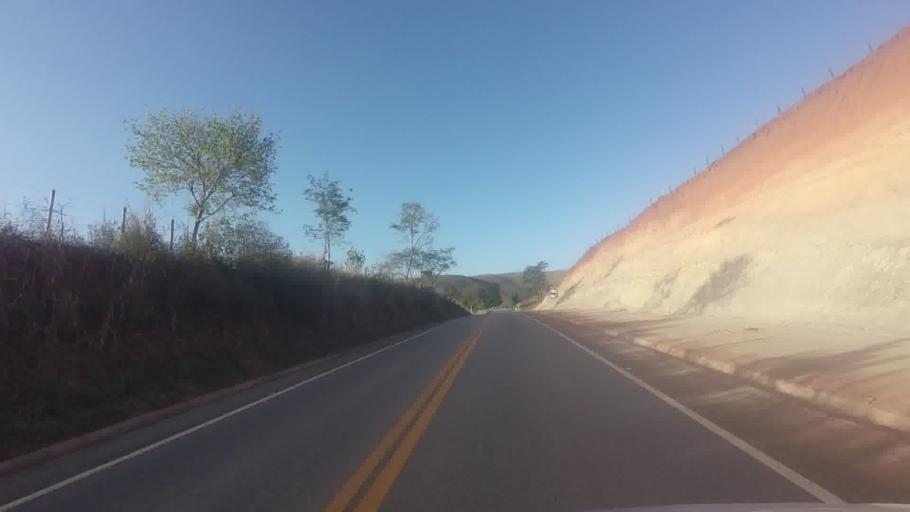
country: BR
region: Espirito Santo
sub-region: Jeronimo Monteiro
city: Jeronimo Monteiro
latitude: -20.8955
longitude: -41.2879
